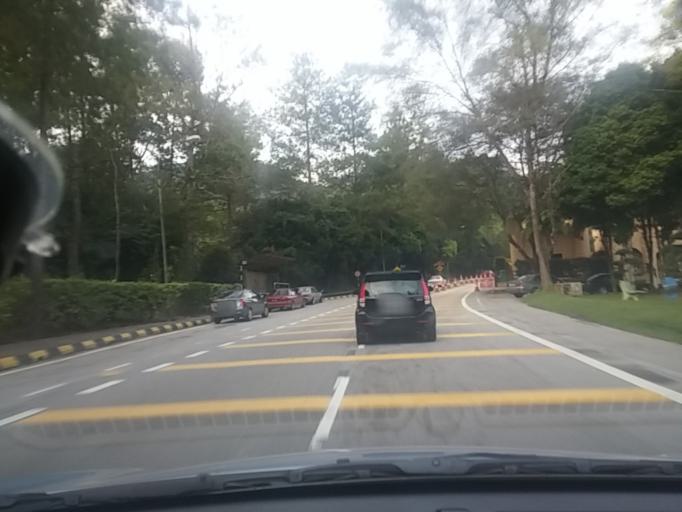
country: MY
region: Pahang
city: Kampung Bukit Tinggi, Bentong
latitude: 3.3996
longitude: 101.7698
